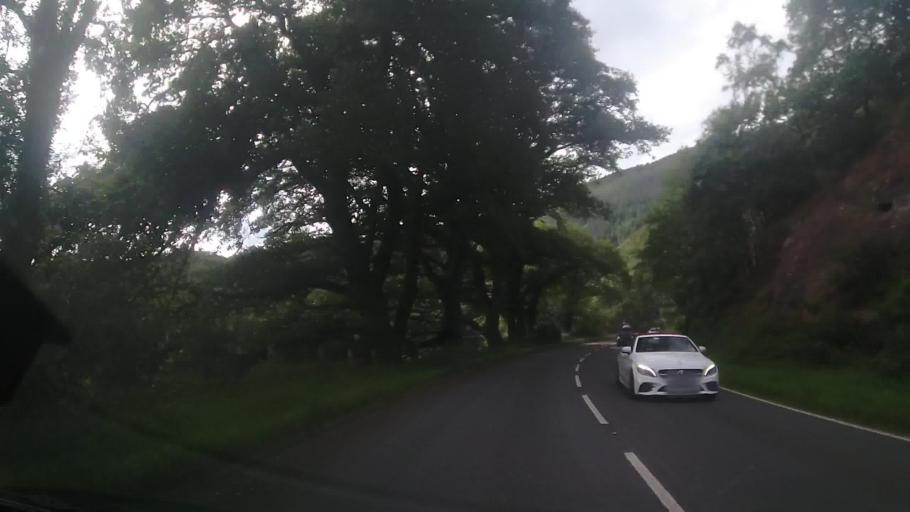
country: GB
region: Wales
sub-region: Gwynedd
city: Barmouth
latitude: 52.7472
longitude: -3.9785
